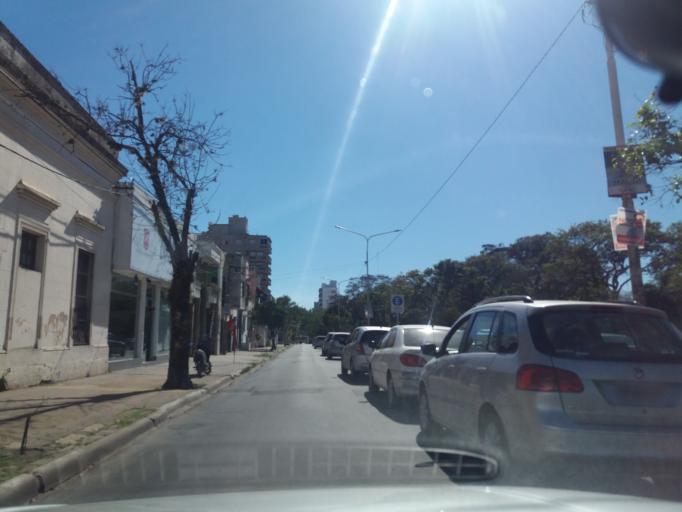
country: AR
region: Corrientes
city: Corrientes
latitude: -27.4716
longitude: -58.8409
